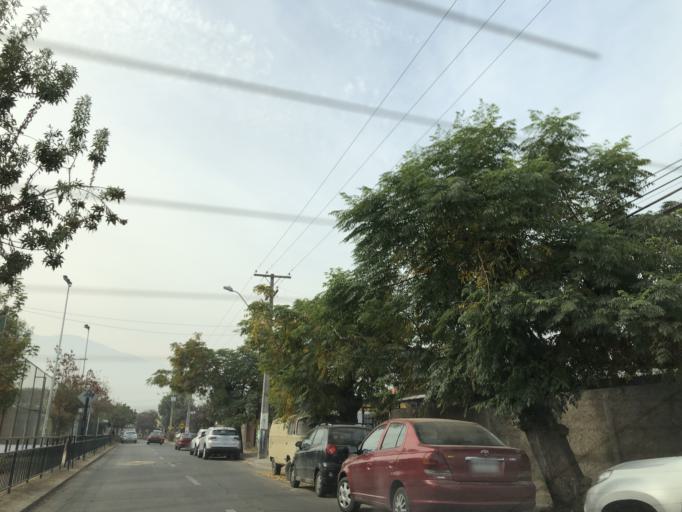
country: CL
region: Santiago Metropolitan
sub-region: Provincia de Cordillera
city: Puente Alto
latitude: -33.5719
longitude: -70.5808
